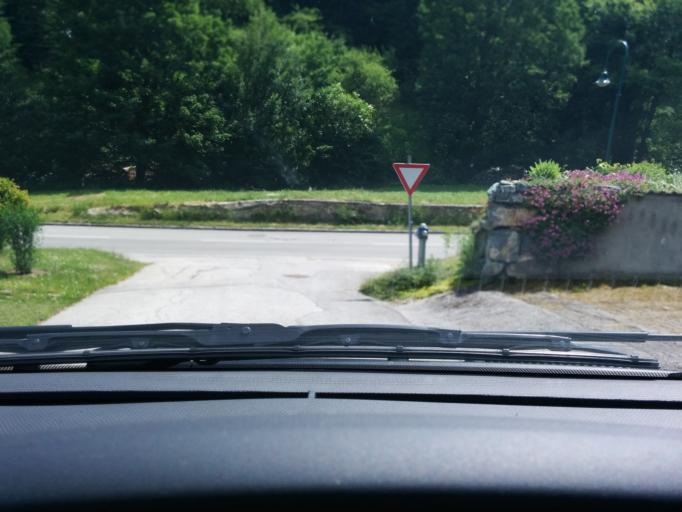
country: AT
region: Lower Austria
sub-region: Politischer Bezirk Wiener Neustadt
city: Miesenbach
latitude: 47.8429
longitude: 15.9818
